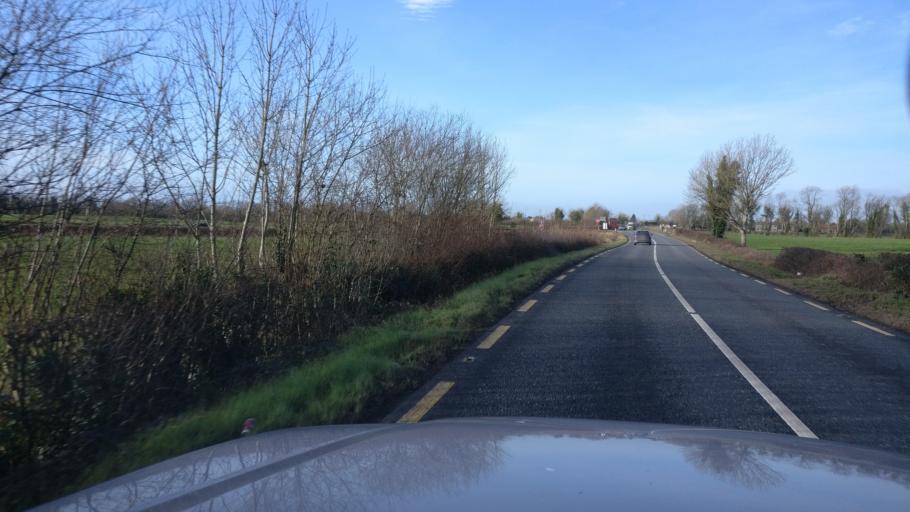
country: IE
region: Leinster
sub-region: Laois
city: Mountmellick
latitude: 53.1458
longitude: -7.3671
